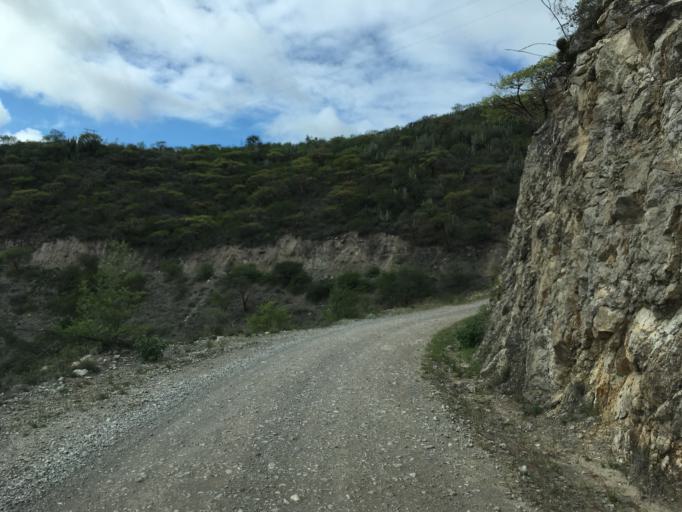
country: MX
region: Hidalgo
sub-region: Metztitlan
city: Fontezuelas
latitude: 20.6413
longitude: -98.9355
